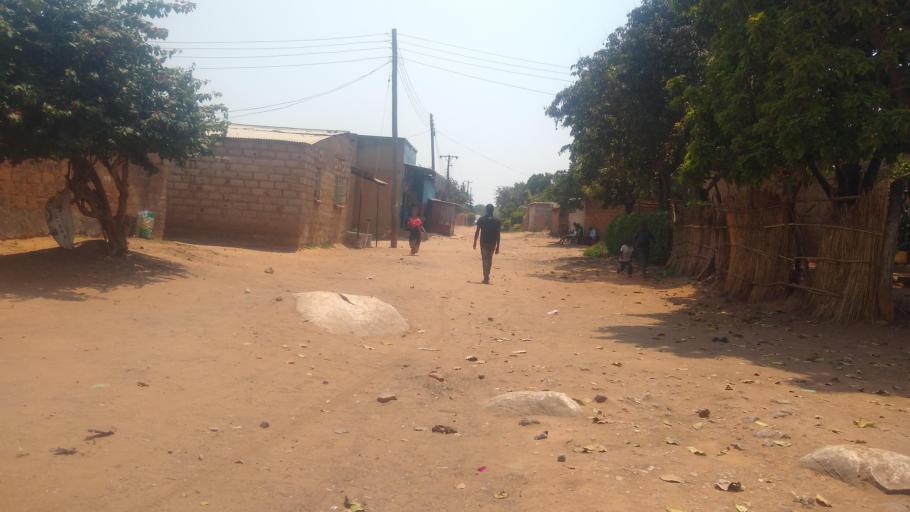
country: ZM
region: Lusaka
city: Lusaka
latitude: -15.4390
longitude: 28.3810
